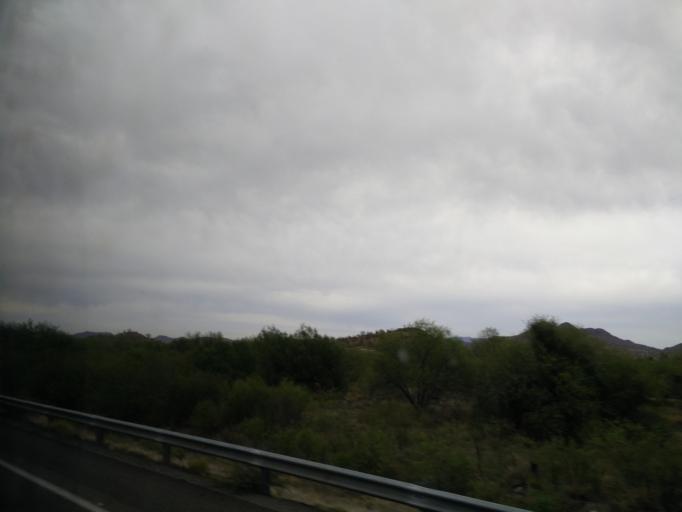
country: MX
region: Sonora
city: Hermosillo
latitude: 28.8721
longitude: -110.9585
